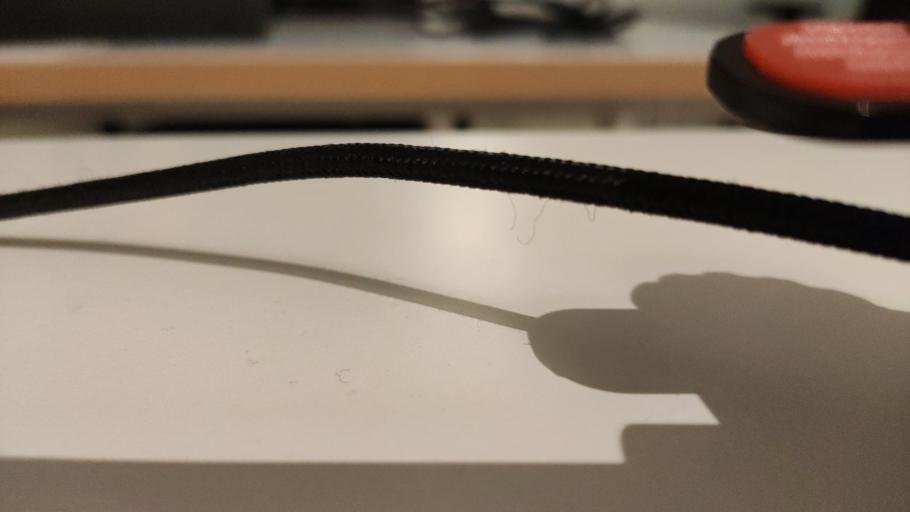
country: RU
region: Moskovskaya
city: Novosin'kovo
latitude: 56.3977
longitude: 37.2672
